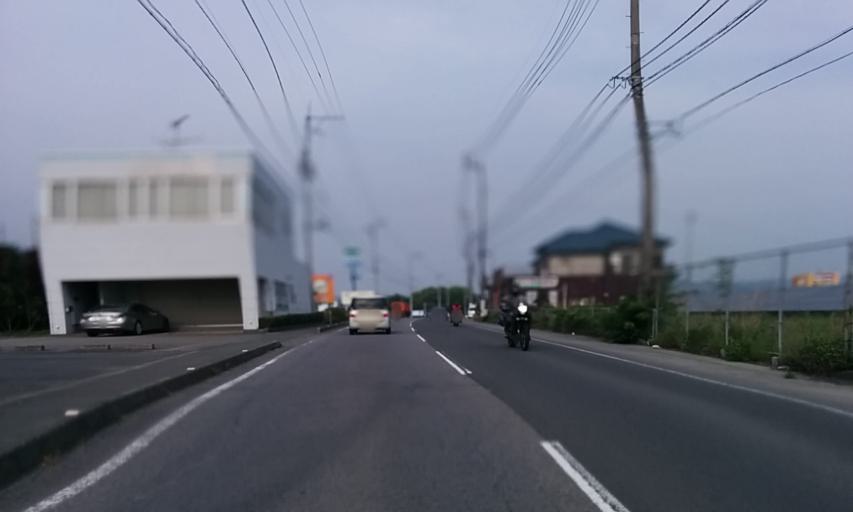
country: JP
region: Ehime
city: Kawanoecho
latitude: 33.9608
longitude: 133.4498
